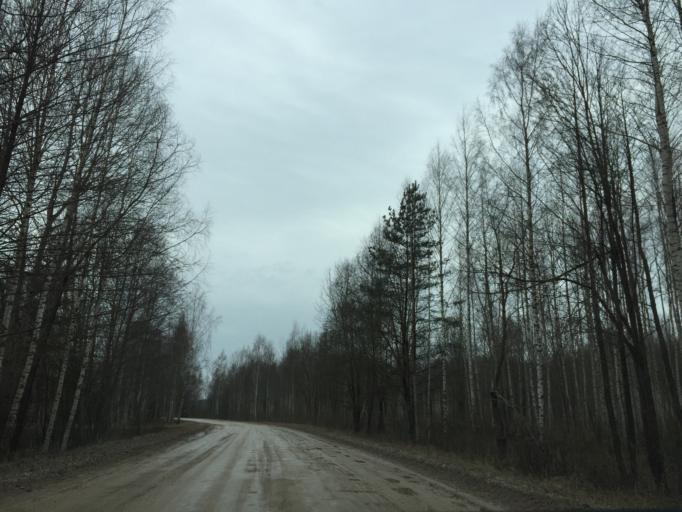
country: LV
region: Ozolnieku
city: Ozolnieki
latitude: 56.7056
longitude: 23.7609
